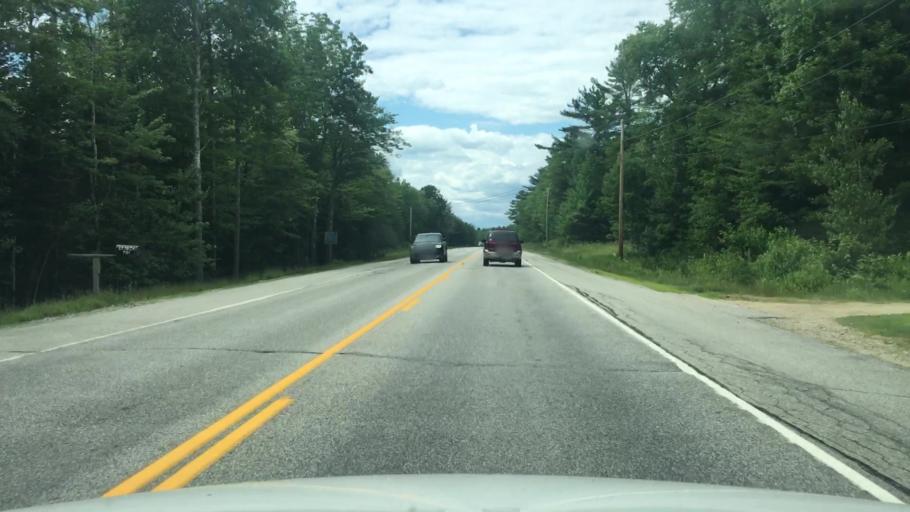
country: US
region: Maine
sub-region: Oxford County
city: West Paris
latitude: 44.3629
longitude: -70.5860
